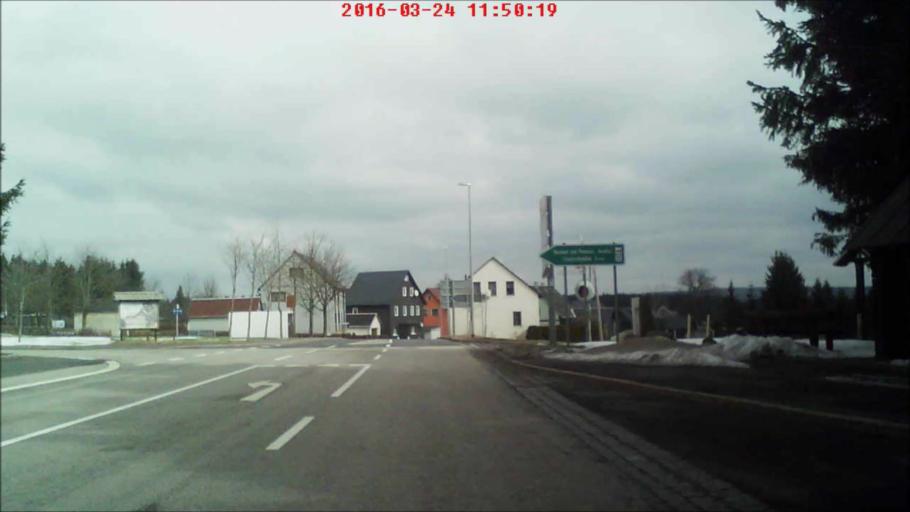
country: DE
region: Thuringia
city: Steinheid
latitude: 50.4664
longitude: 11.0391
